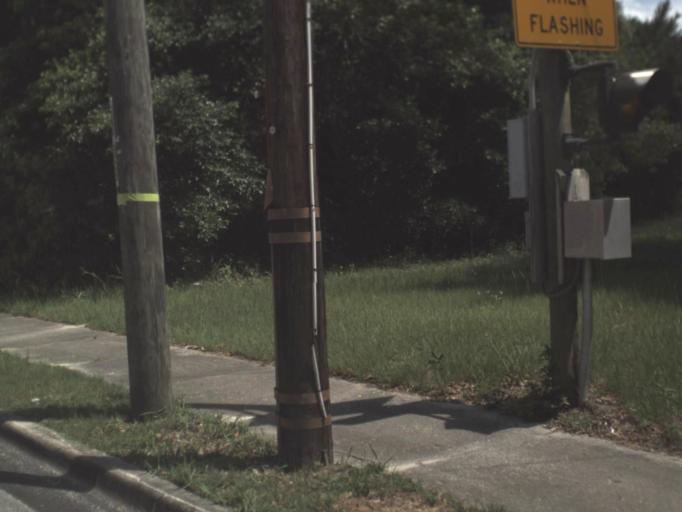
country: US
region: Florida
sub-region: Alachua County
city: High Springs
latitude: 29.8312
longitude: -82.6066
